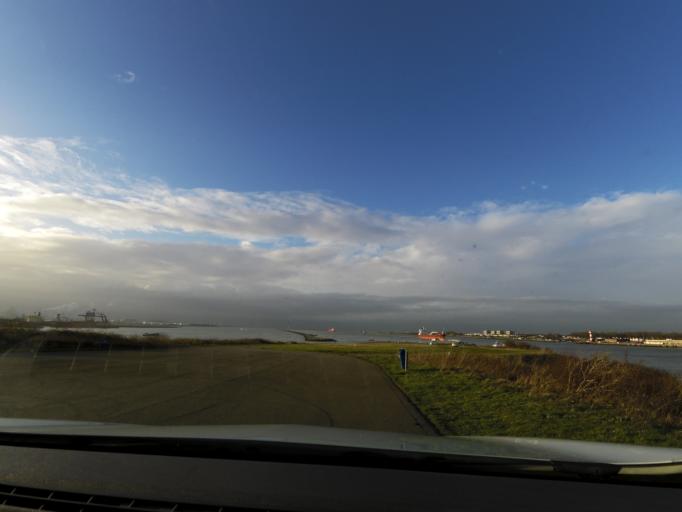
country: NL
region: South Holland
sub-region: Gemeente Rotterdam
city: Hoek van Holland
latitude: 51.9669
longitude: 4.1300
